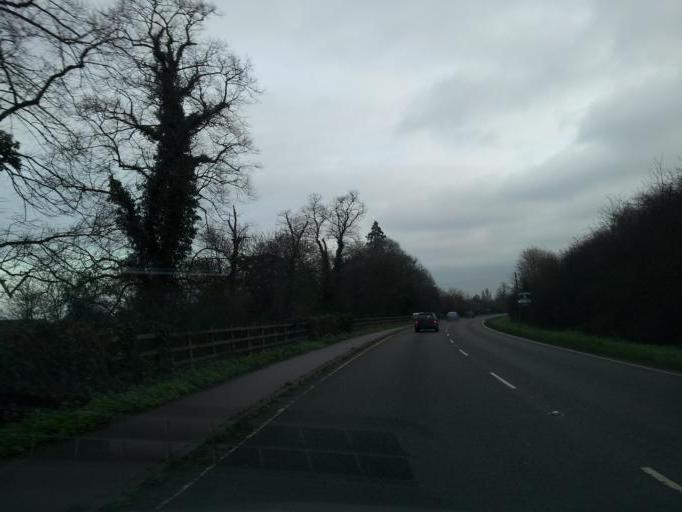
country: GB
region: England
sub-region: Cambridgeshire
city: Grantchester
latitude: 52.1965
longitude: 0.0861
